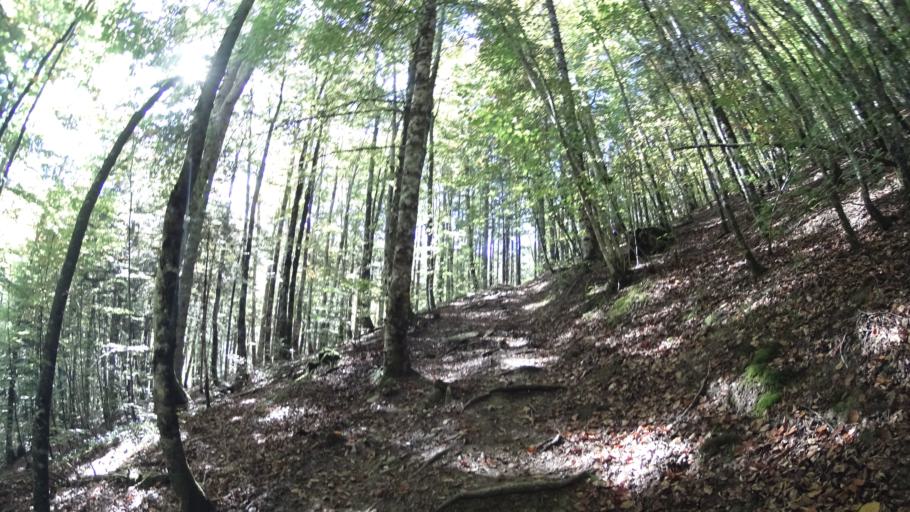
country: ES
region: Navarre
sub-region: Provincia de Navarra
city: Oronz
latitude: 42.9866
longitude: -1.1105
